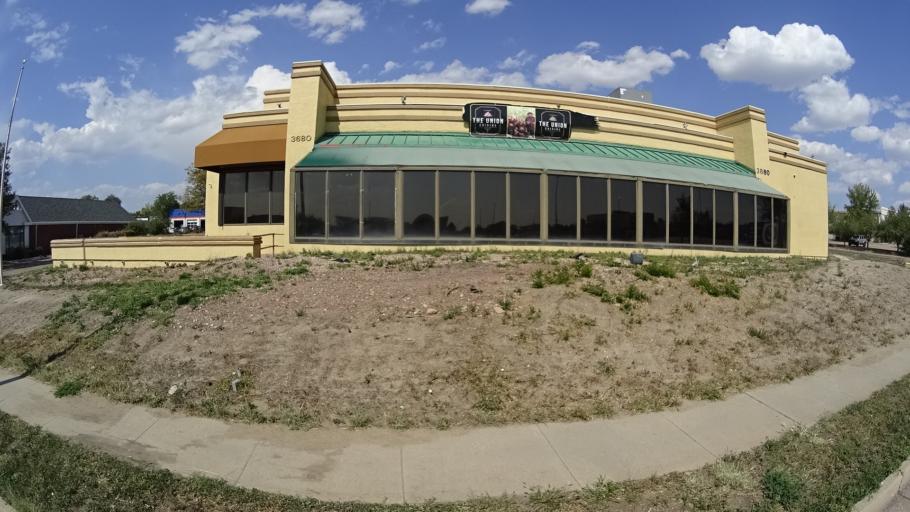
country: US
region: Colorado
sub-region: El Paso County
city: Colorado Springs
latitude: 38.8459
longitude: -104.7604
